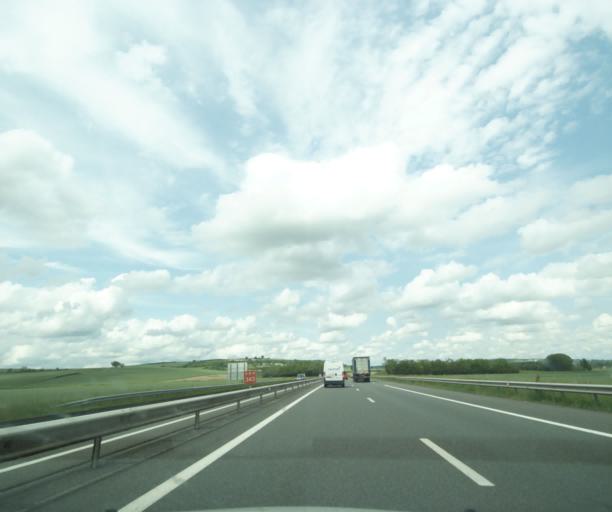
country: FR
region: Auvergne
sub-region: Departement de l'Allier
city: Ebreuil
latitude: 46.1447
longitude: 3.1137
